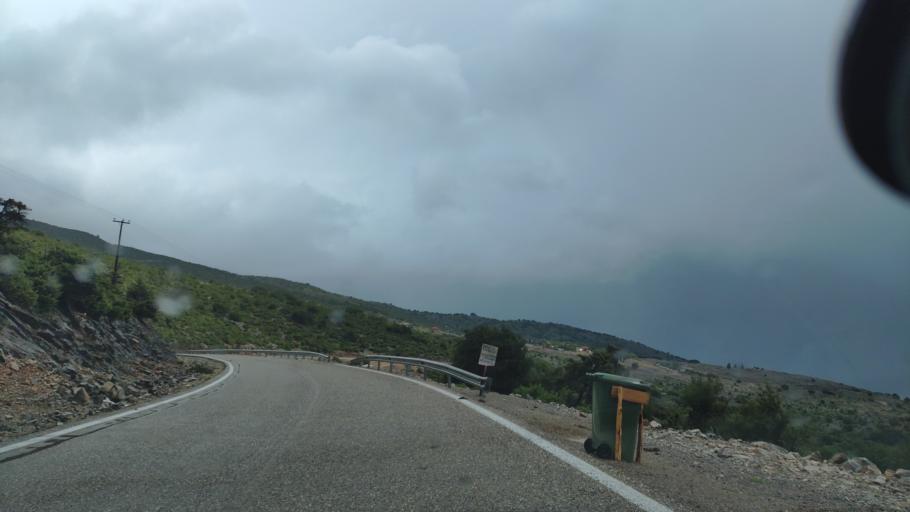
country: GR
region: West Greece
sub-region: Nomos Aitolias kai Akarnanias
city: Krikellos
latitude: 39.0694
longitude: 21.3840
